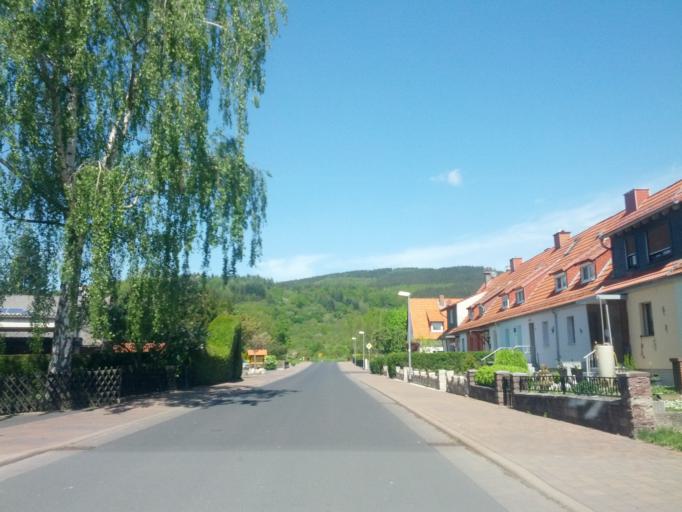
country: DE
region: Hesse
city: Witzenhausen
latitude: 51.3437
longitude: 9.8826
